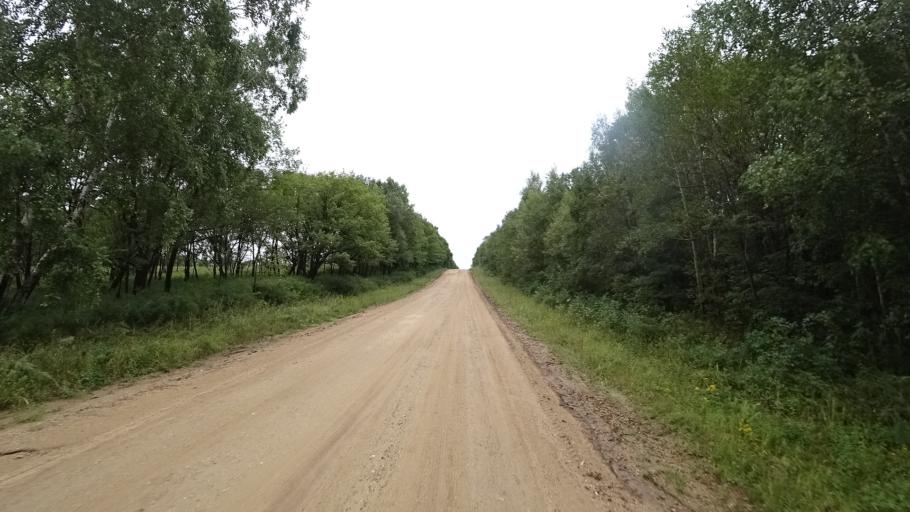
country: RU
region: Primorskiy
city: Ivanovka
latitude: 44.0461
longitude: 132.5445
